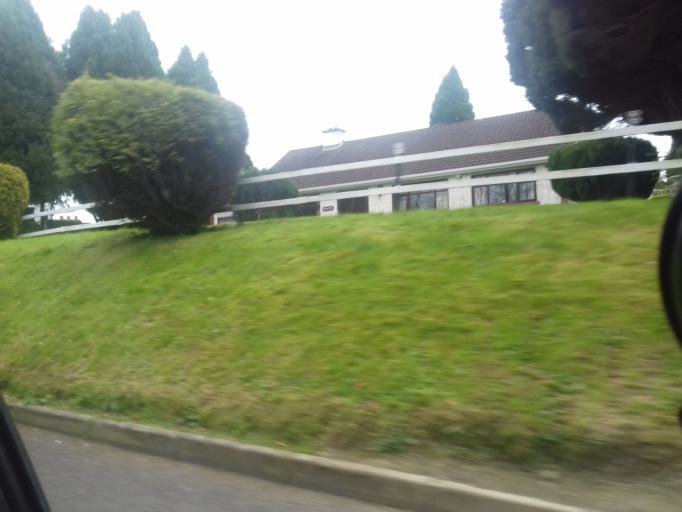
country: IE
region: Leinster
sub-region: An Iarmhi
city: An Muileann gCearr
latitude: 53.5257
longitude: -7.3263
